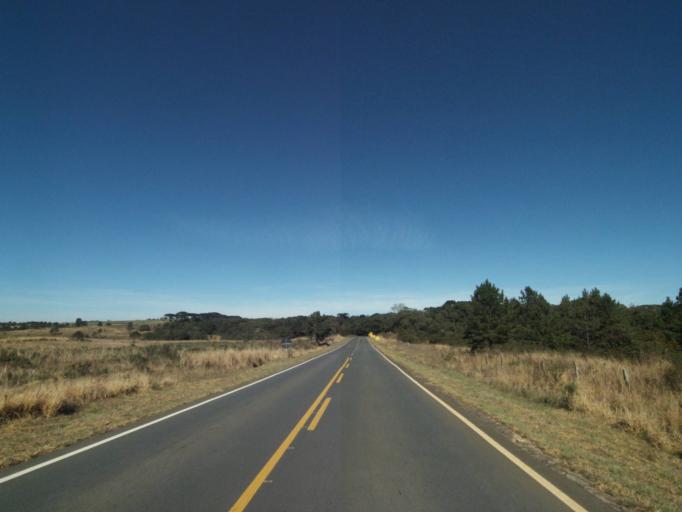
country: BR
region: Parana
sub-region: Castro
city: Castro
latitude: -24.7255
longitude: -50.1853
